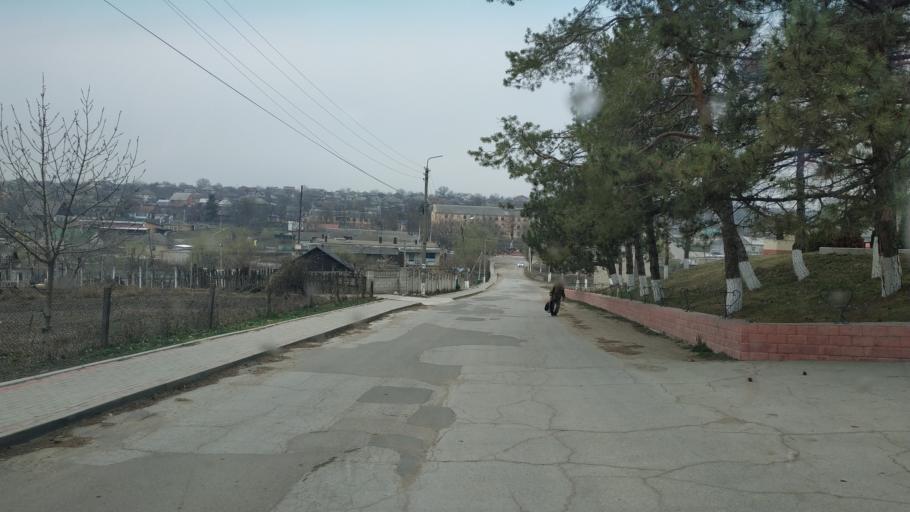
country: MD
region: Chisinau
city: Singera
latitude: 46.8231
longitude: 29.0401
